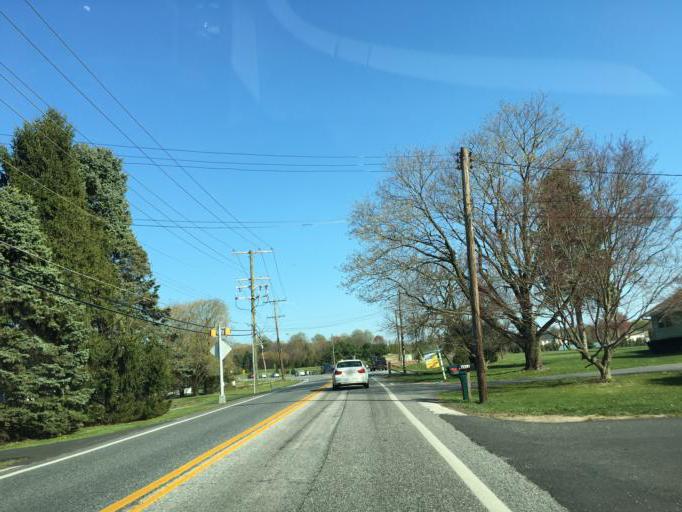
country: US
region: Maryland
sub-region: Baltimore County
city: Hunt Valley
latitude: 39.5145
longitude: -76.5556
